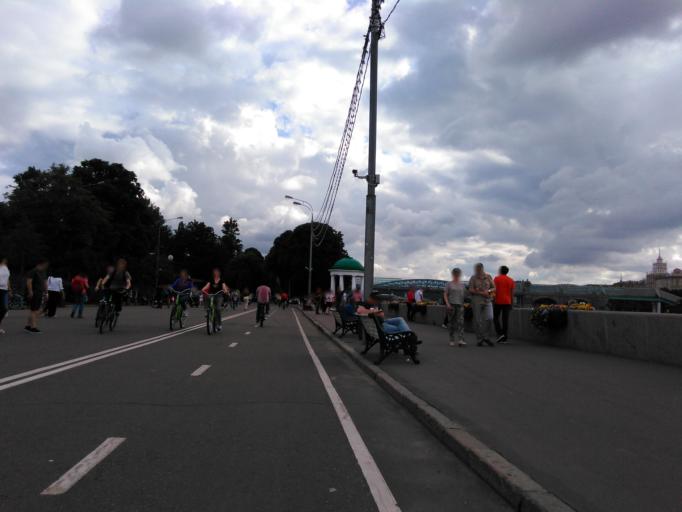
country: RU
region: Moscow
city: Novyye Cheremushki
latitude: 55.7278
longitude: 37.5963
